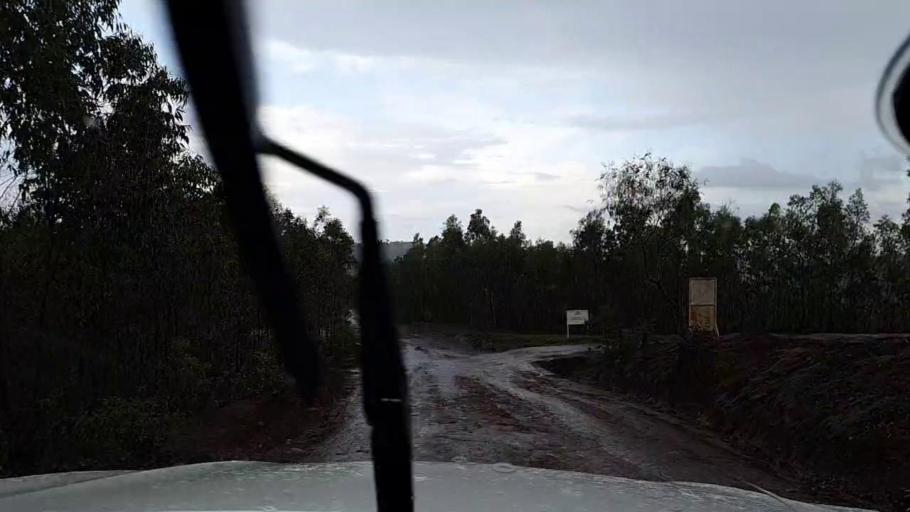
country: BI
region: Kayanza
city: Kayanza
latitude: -2.7755
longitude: 29.5428
